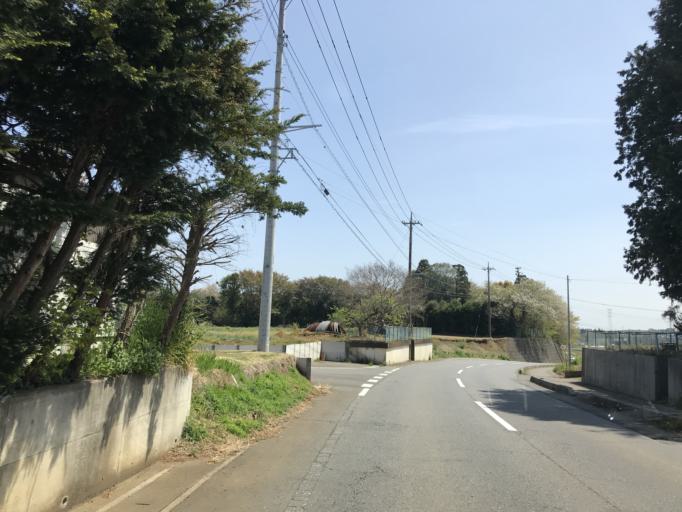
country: JP
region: Ibaraki
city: Naka
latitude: 36.0449
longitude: 140.0741
